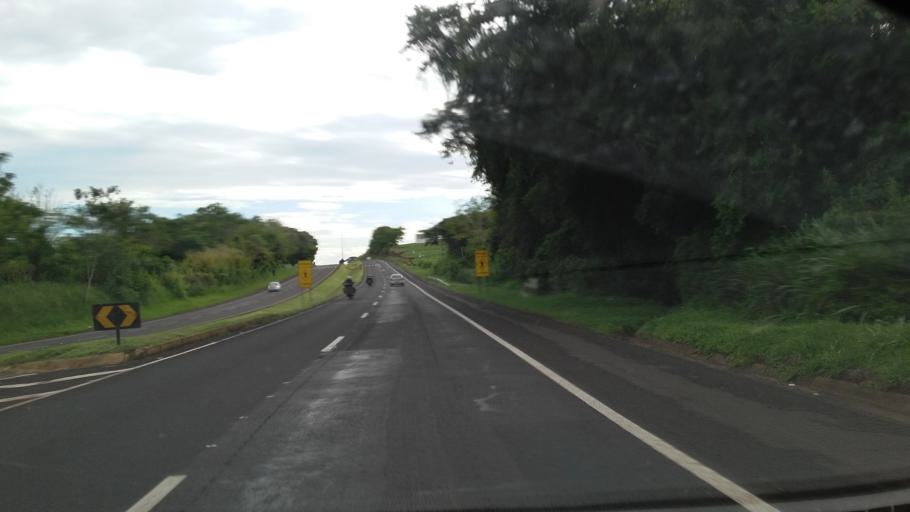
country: BR
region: Parana
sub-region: Paicandu
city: Paicandu
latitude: -23.5126
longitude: -52.0254
